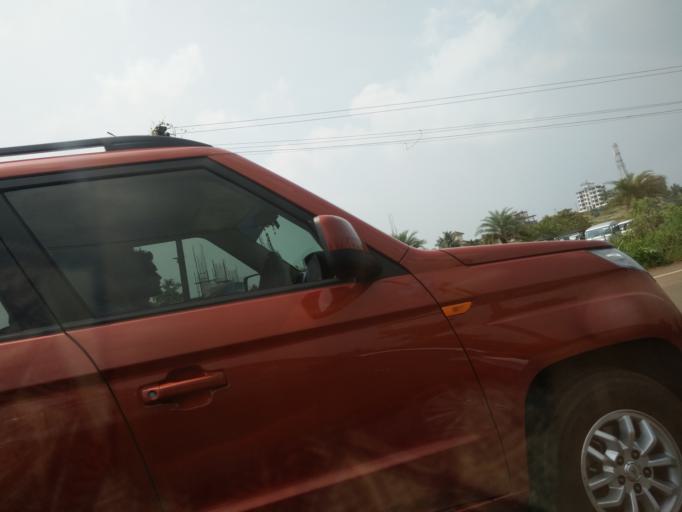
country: IN
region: Goa
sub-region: South Goa
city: Sancoale
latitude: 15.3767
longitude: 73.9257
